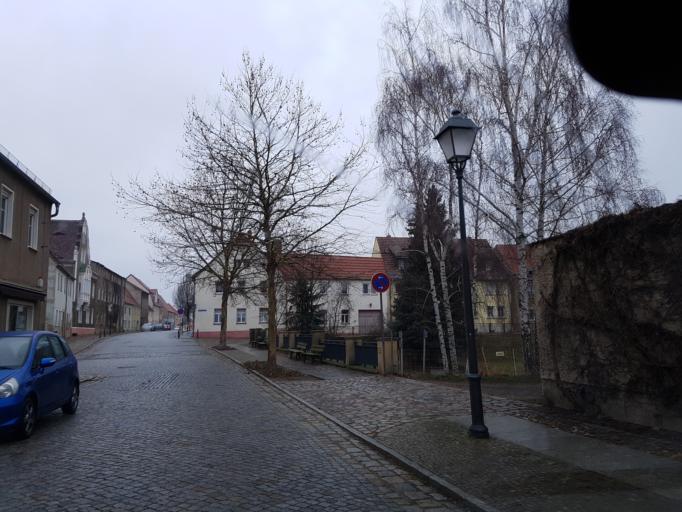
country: DE
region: Brandenburg
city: Muhlberg
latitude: 51.4334
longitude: 13.2154
